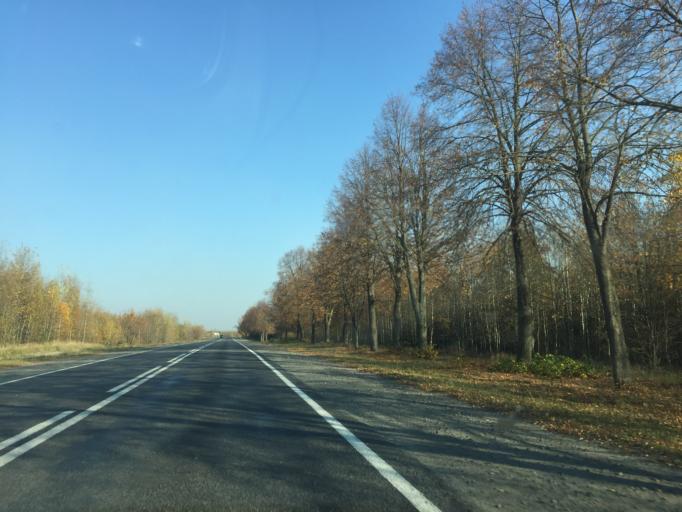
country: BY
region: Gomel
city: Dobrush
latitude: 52.3878
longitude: 31.4480
